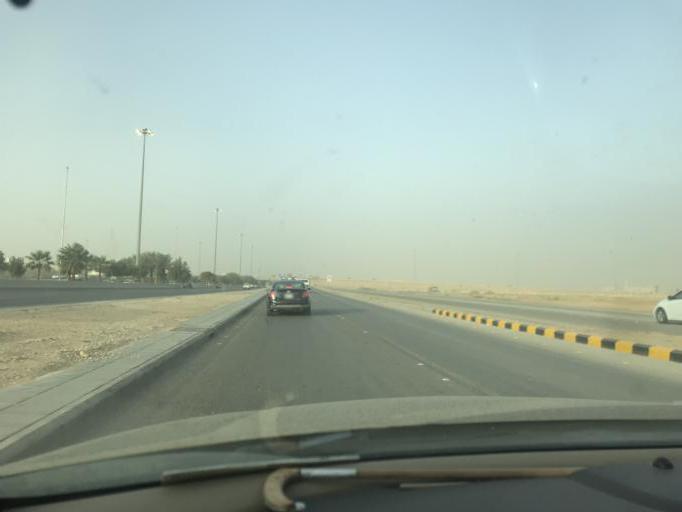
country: SA
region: Ar Riyad
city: Riyadh
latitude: 24.8376
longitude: 46.6395
